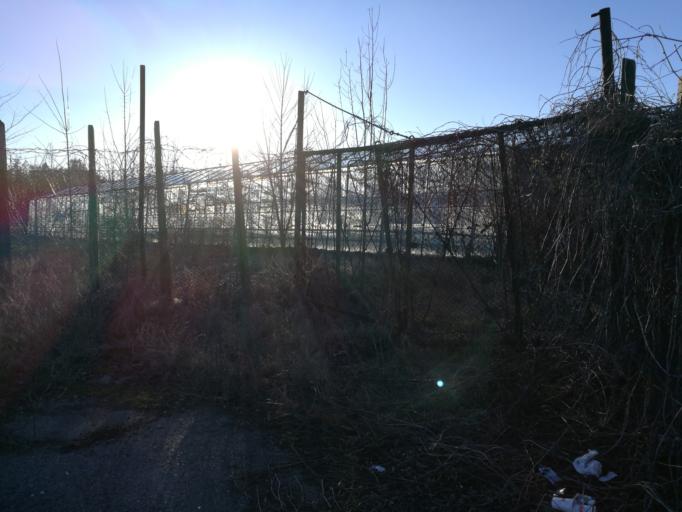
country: RO
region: Ilfov
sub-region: Comuna Otopeni
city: Otopeni
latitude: 44.5015
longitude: 26.0767
